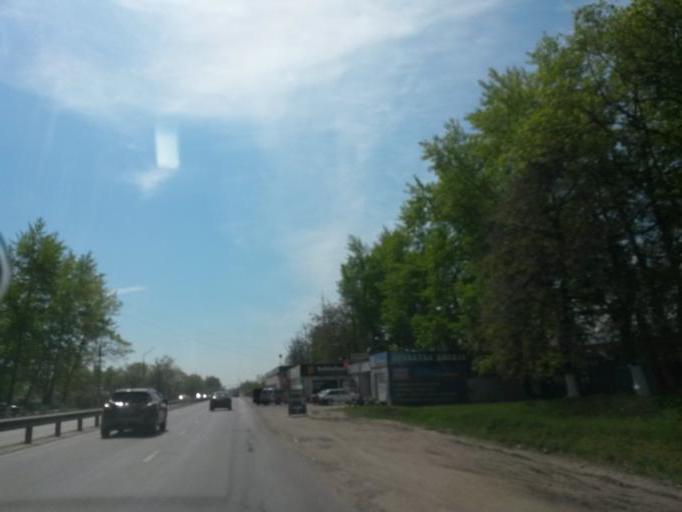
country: RU
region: Moskovskaya
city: Shcherbinka
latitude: 55.4722
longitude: 37.5625
